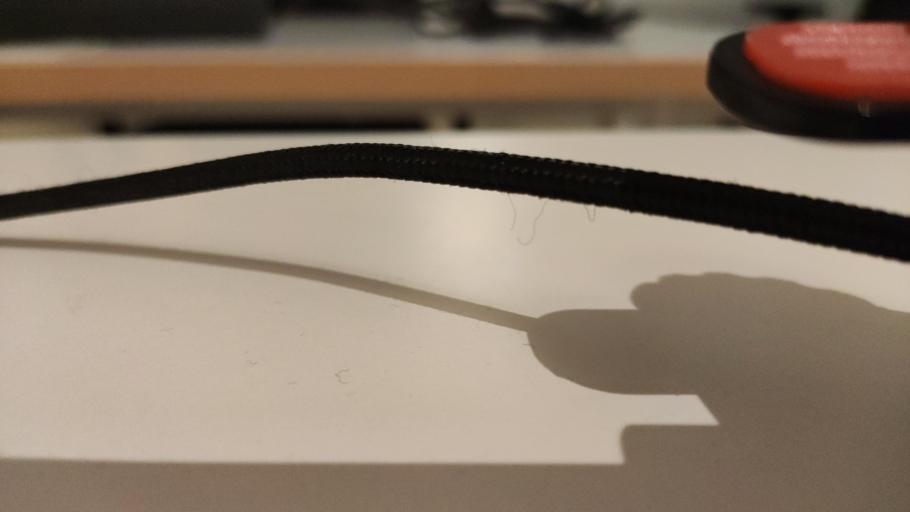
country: RU
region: Moskovskaya
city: Il'inskiy Pogost
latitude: 55.4998
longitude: 38.8736
